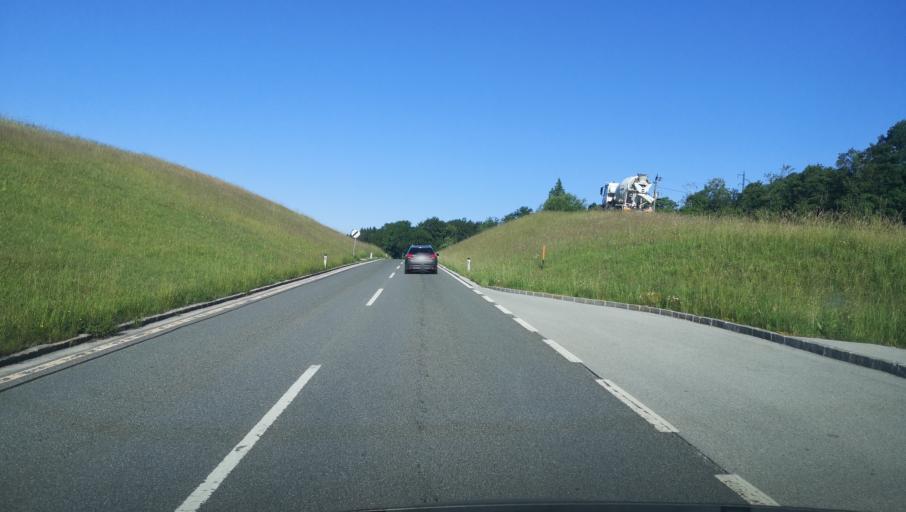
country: AT
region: Lower Austria
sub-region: Politischer Bezirk Scheibbs
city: Randegg
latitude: 47.9724
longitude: 14.9734
